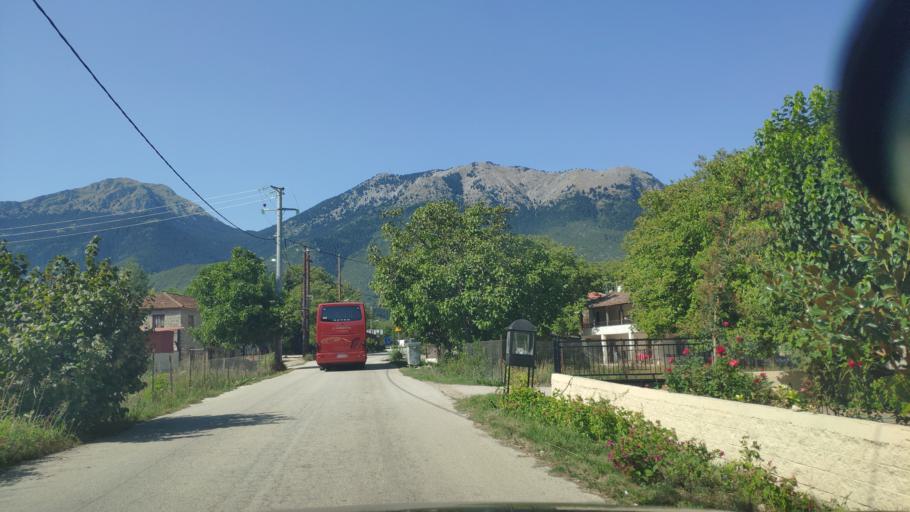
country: GR
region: Peloponnese
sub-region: Nomos Korinthias
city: Nemea
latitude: 37.8452
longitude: 22.4089
